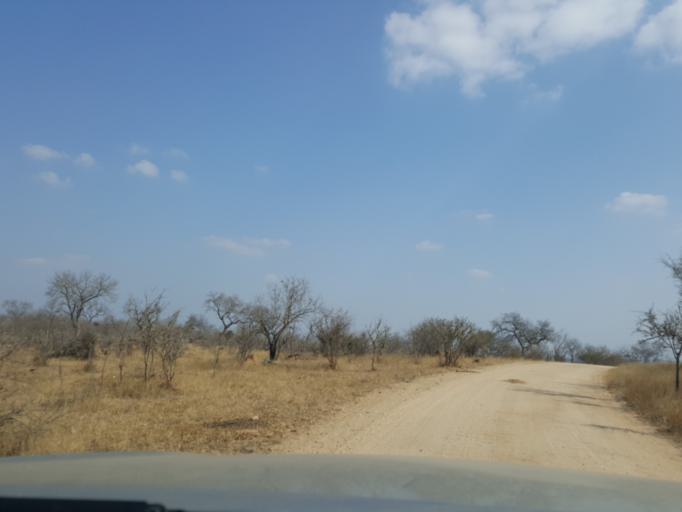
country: ZA
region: Mpumalanga
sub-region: Ehlanzeni District
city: Komatipoort
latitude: -25.2726
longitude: 31.7909
